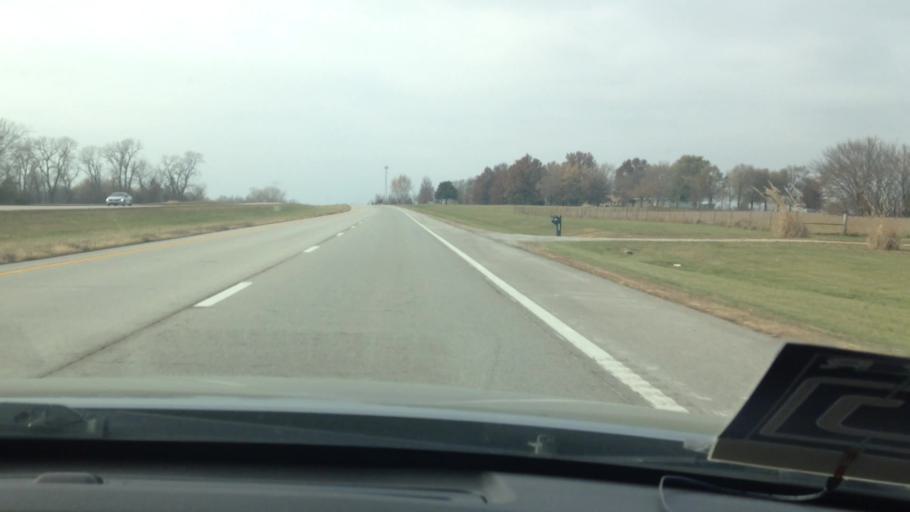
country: US
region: Missouri
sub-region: Cass County
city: Garden City
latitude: 38.5438
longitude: -94.1654
